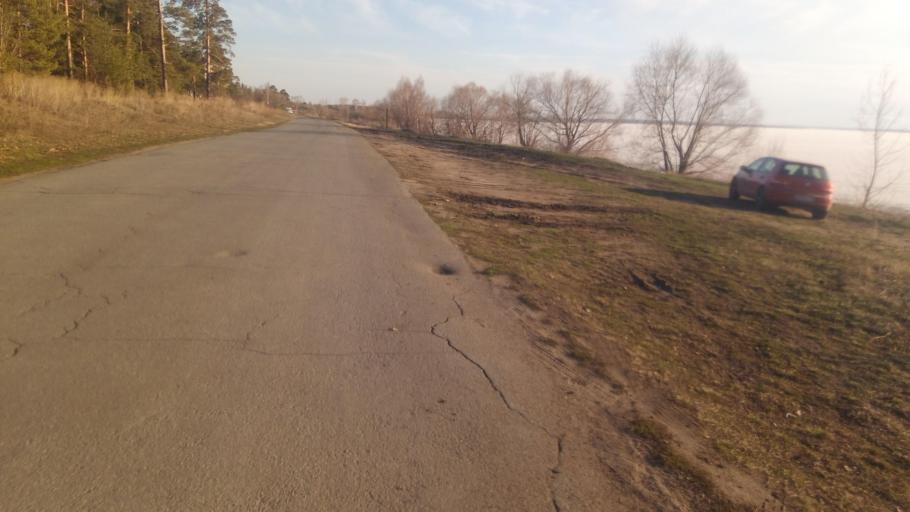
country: RU
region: Chelyabinsk
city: Novosineglazovskiy
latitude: 55.1293
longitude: 61.3282
